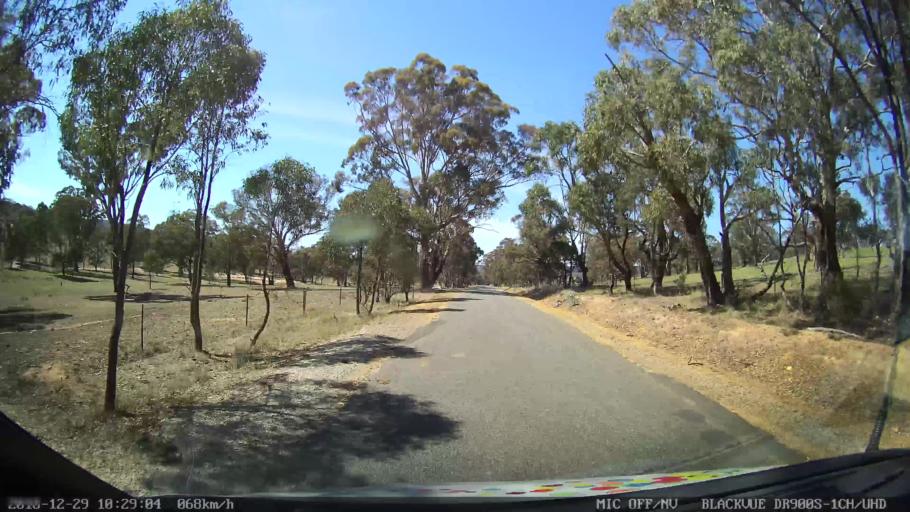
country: AU
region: New South Wales
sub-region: Yass Valley
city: Gundaroo
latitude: -34.9483
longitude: 149.4567
